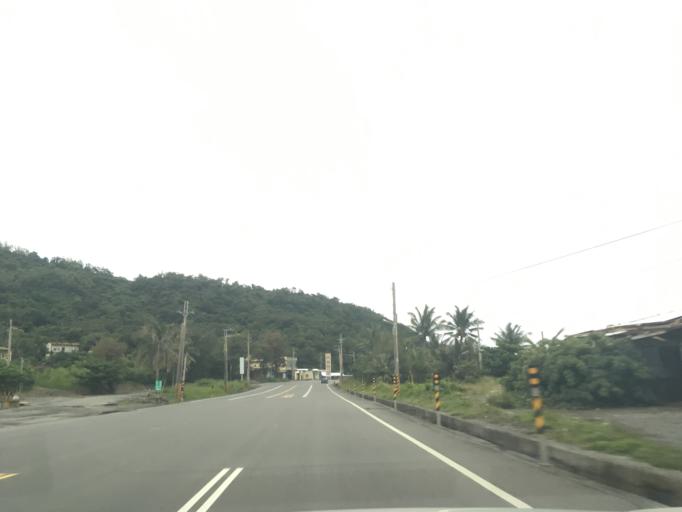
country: TW
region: Taiwan
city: Hengchun
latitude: 22.3287
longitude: 120.8922
